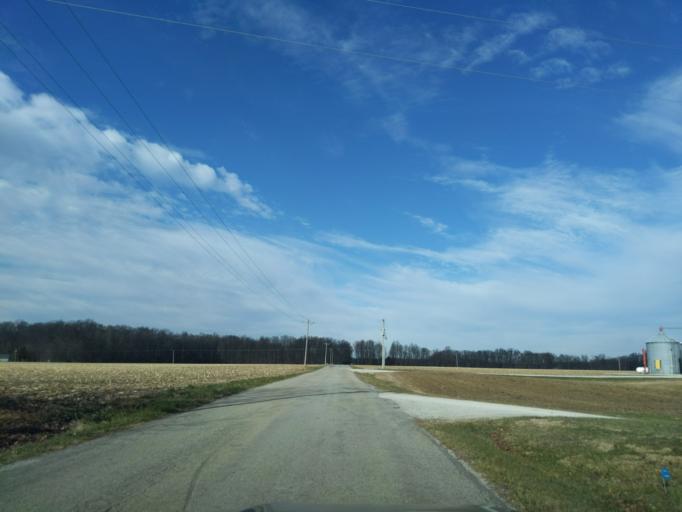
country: US
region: Indiana
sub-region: Decatur County
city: Greensburg
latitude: 39.2753
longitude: -85.4234
